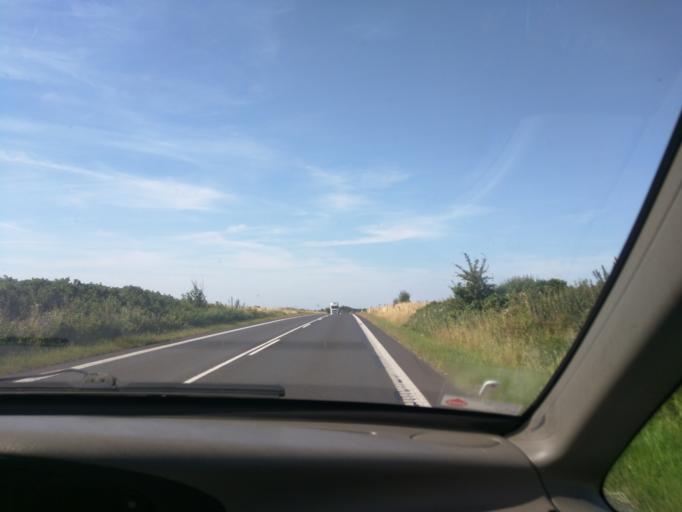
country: DK
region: Central Jutland
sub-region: Viborg Kommune
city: Bjerringbro
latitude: 56.3528
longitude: 9.6773
